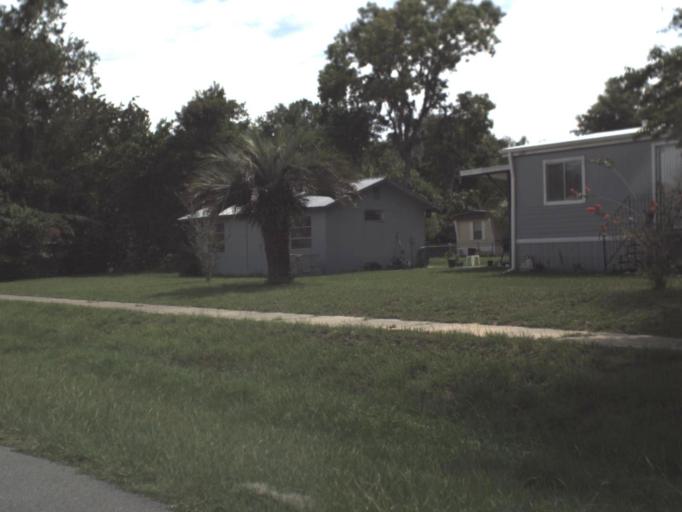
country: US
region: Florida
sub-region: Citrus County
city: Hernando
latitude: 28.9299
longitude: -82.3770
